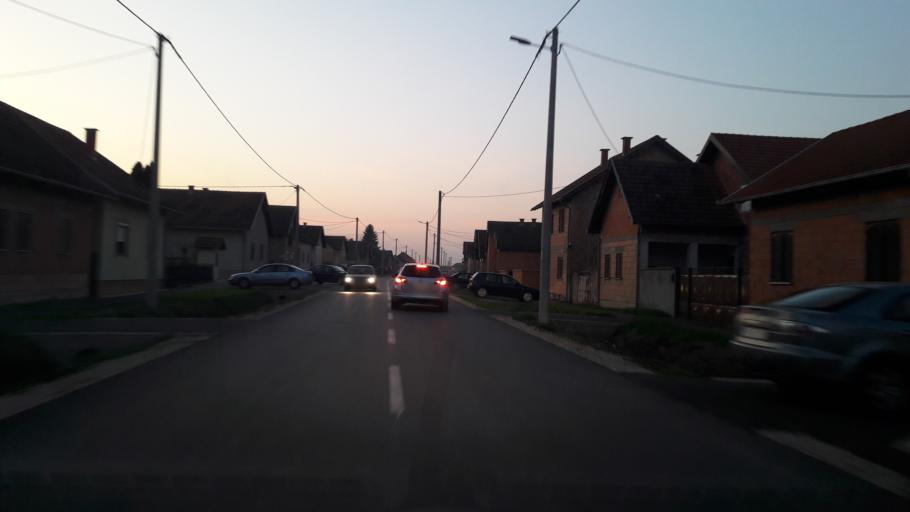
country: HR
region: Vukovarsko-Srijemska
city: Nijemci
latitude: 45.1415
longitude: 19.0339
